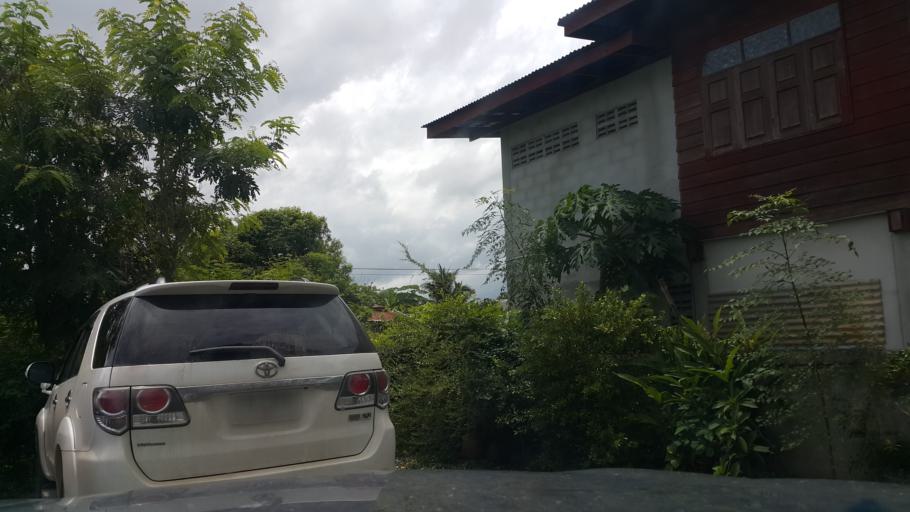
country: TH
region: Sukhothai
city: Thung Saliam
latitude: 17.3198
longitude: 99.5497
